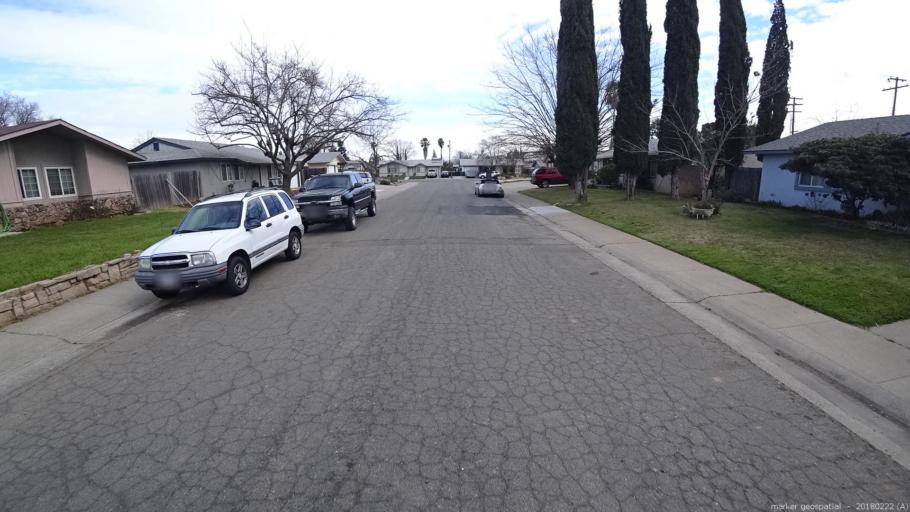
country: US
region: California
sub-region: Sacramento County
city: Rio Linda
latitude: 38.7135
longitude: -121.4145
